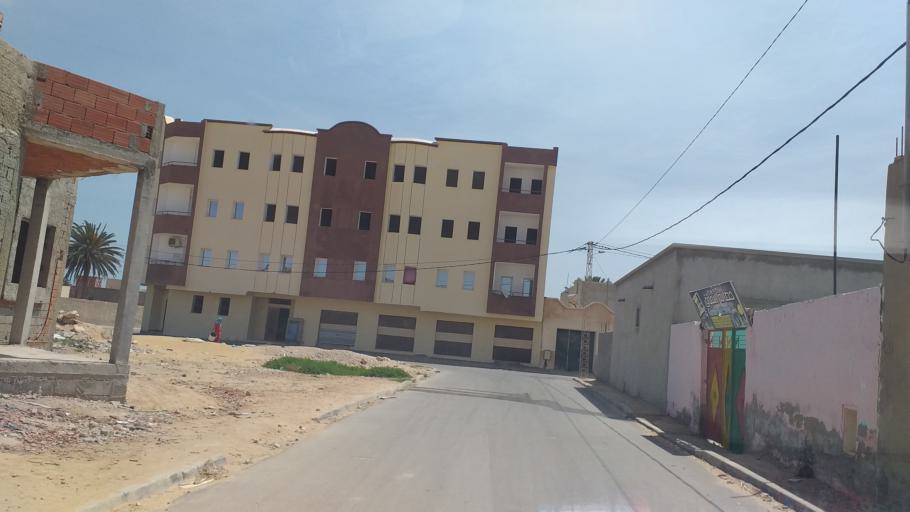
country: TN
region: Qabis
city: Gabes
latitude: 33.9475
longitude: 10.0669
